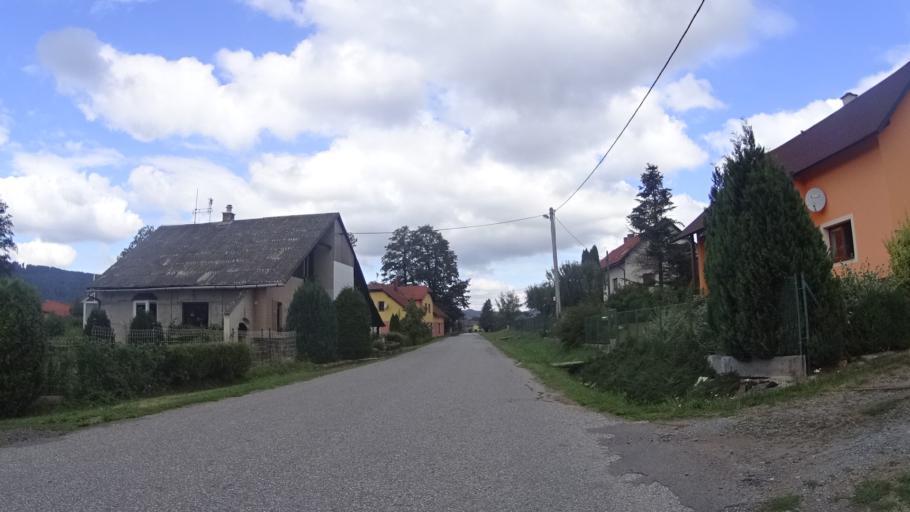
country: CZ
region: Pardubicky
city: Dolni Cermna
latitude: 49.9264
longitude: 16.5469
